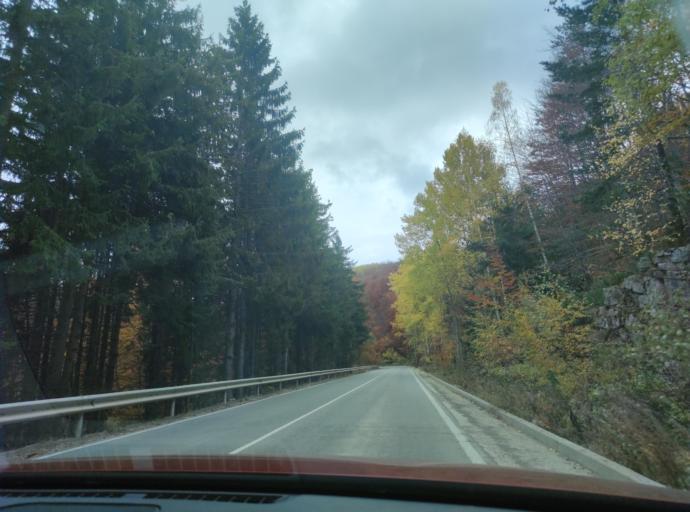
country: BG
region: Sofiya
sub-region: Obshtina Godech
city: Godech
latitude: 43.1097
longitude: 23.1105
